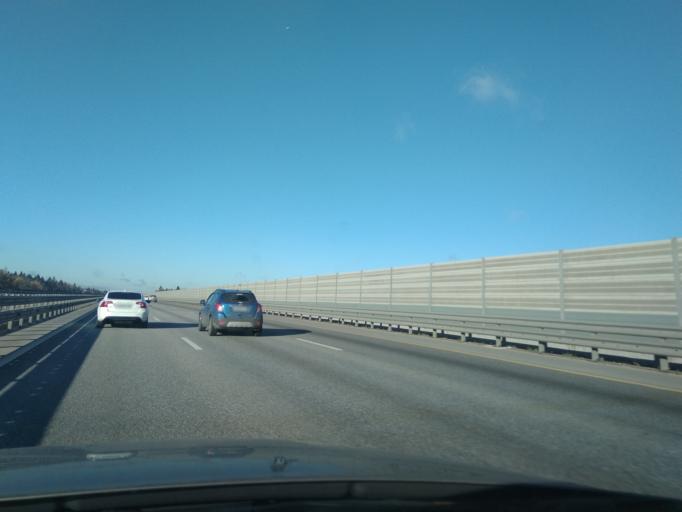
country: RU
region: Moskovskaya
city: Yershovo
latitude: 55.8289
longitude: 36.8814
